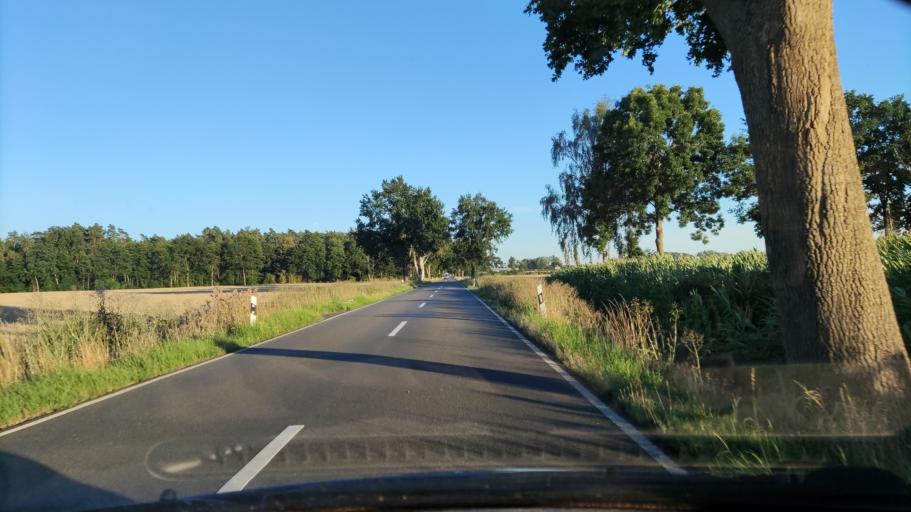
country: DE
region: Lower Saxony
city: Luechow
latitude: 53.0219
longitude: 11.1446
